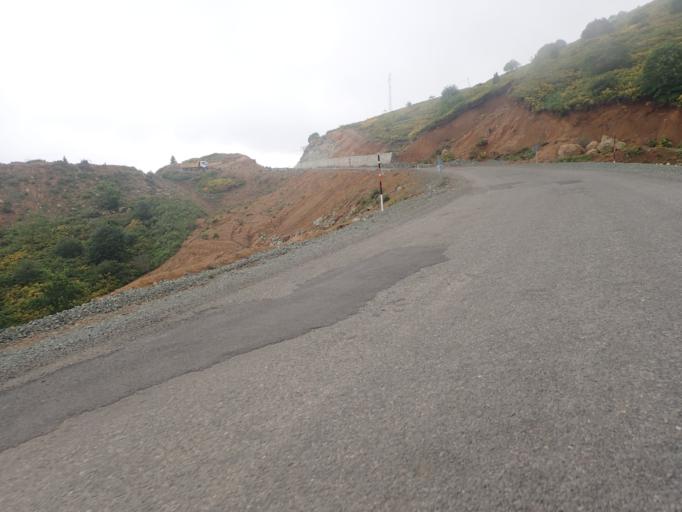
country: TR
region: Ordu
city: Topcam
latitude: 40.6607
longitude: 37.9382
